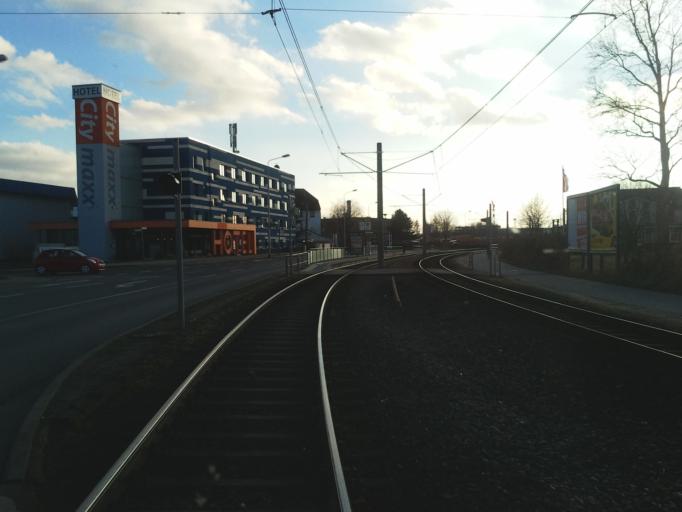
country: DE
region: Mecklenburg-Vorpommern
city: Dierkow-West
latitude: 54.0934
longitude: 12.1577
